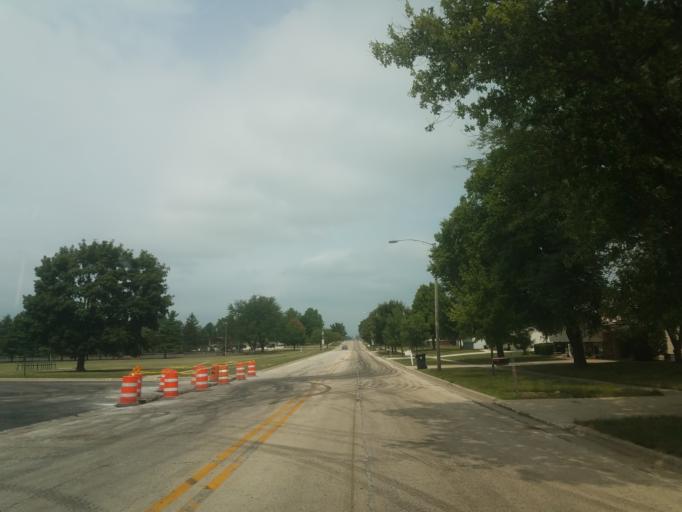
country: US
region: Illinois
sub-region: McLean County
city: Normal
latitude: 40.5127
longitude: -89.0211
